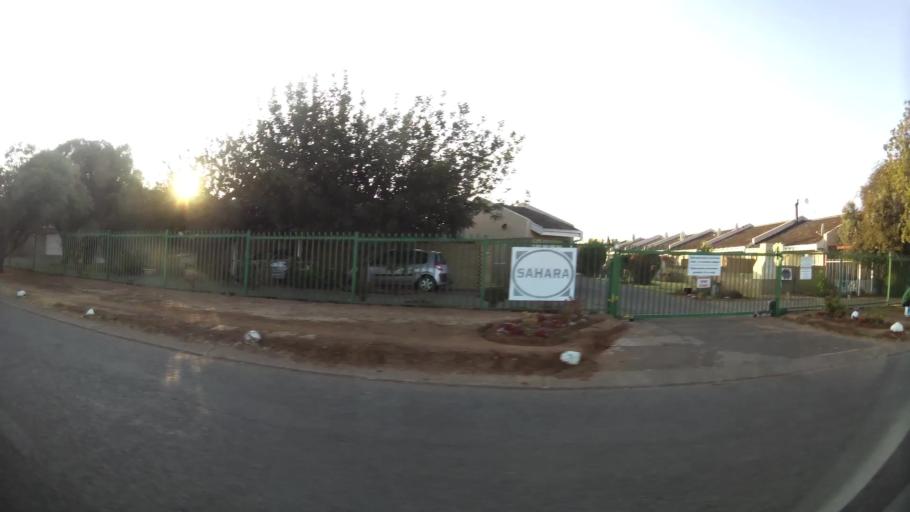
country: ZA
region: Orange Free State
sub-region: Mangaung Metropolitan Municipality
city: Bloemfontein
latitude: -29.0996
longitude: 26.1602
